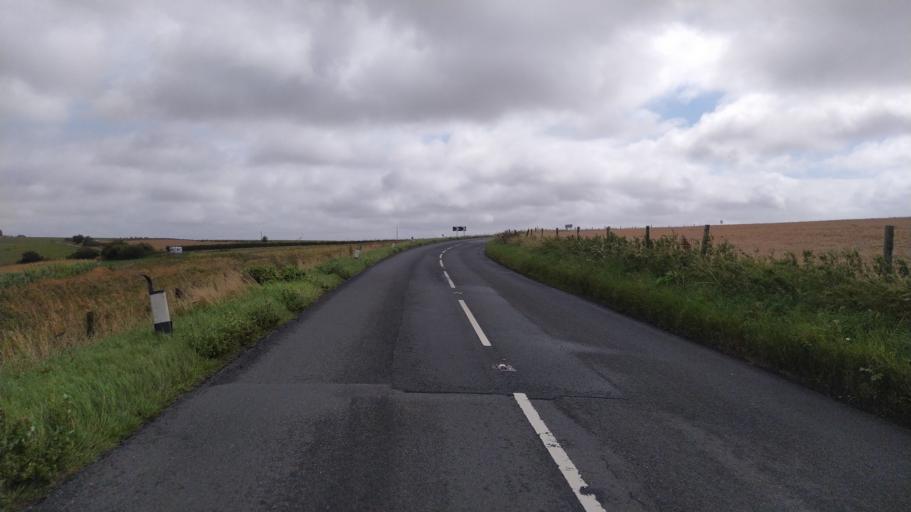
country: GB
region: England
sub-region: Dorset
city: Shaftesbury
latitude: 50.9812
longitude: -2.1220
